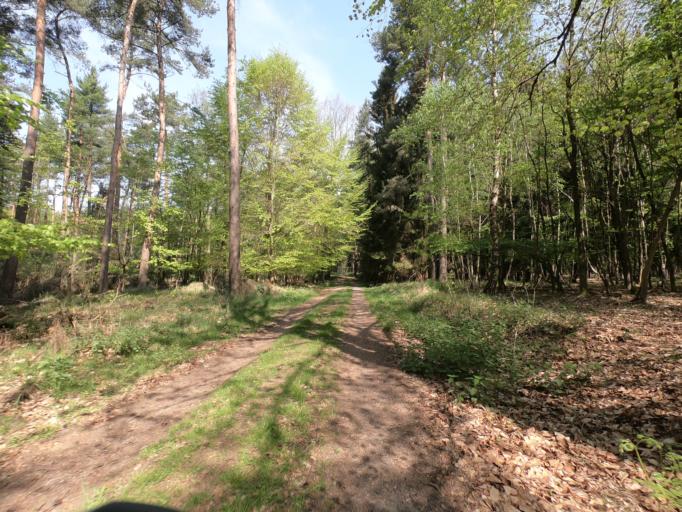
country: DE
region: Hesse
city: Morfelden-Walldorf
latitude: 50.0159
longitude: 8.5462
